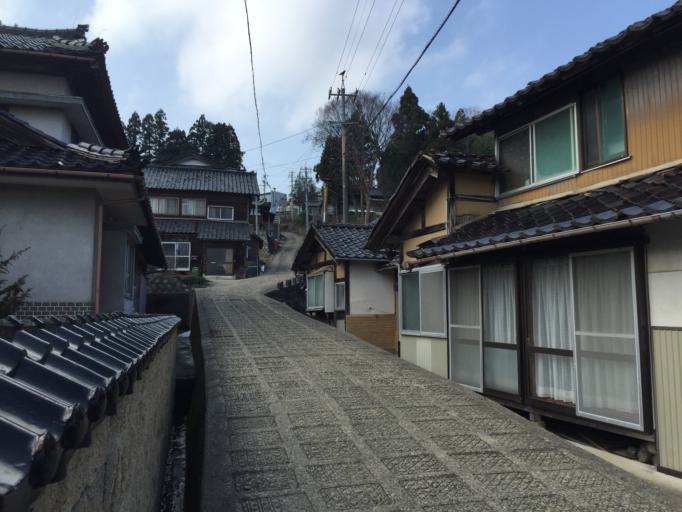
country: JP
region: Ishikawa
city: Nanao
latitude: 37.1361
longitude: 136.9996
